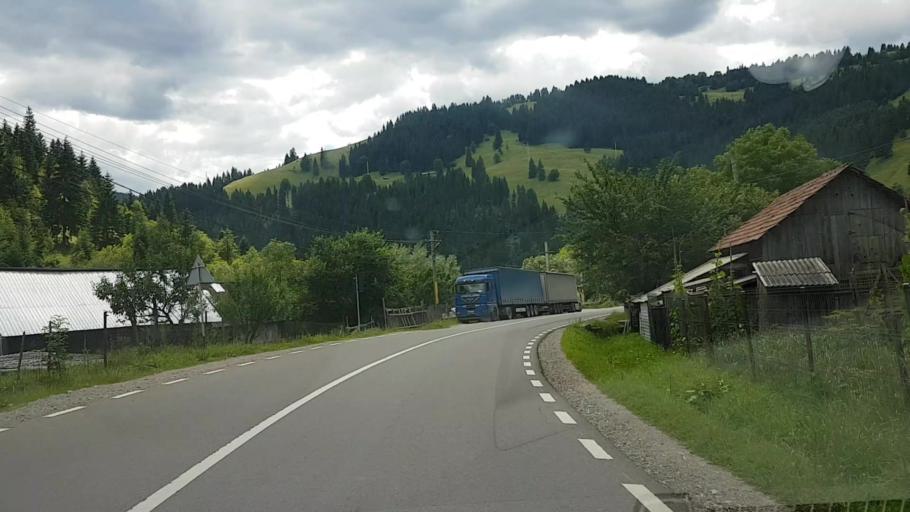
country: RO
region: Neamt
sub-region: Comuna Farcasa
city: Farcasa
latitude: 47.1453
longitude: 25.8640
